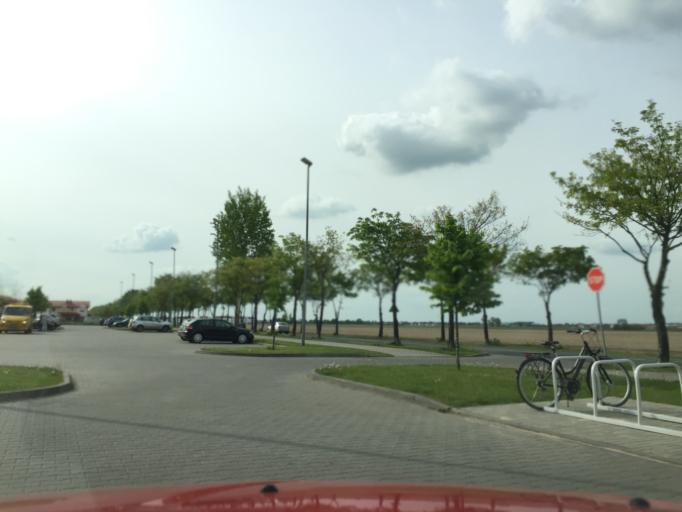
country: PL
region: Greater Poland Voivodeship
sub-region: Powiat poznanski
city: Plewiska
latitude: 52.3908
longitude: 16.7765
